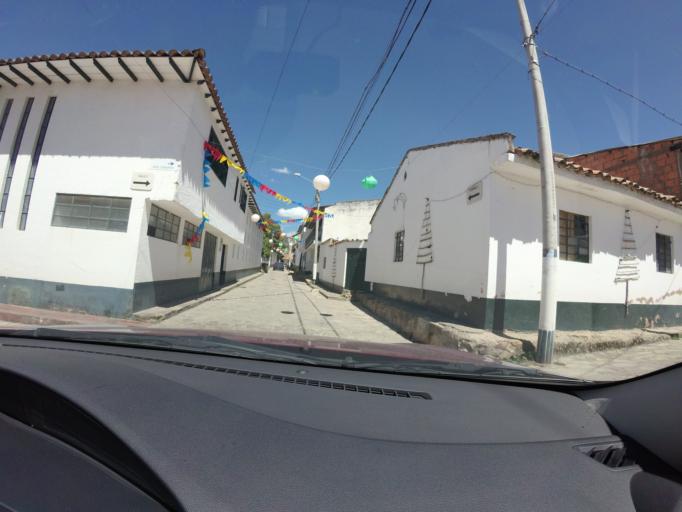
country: CO
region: Cundinamarca
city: Cucunuba
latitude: 5.2488
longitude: -73.7667
